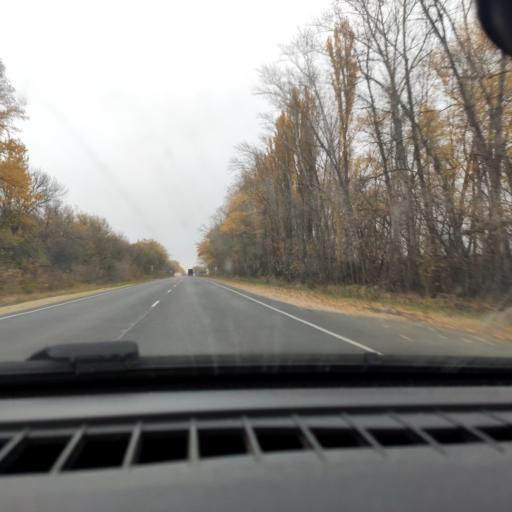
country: RU
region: Voronezj
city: Uryv-Pokrovka
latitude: 51.1657
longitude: 39.0717
